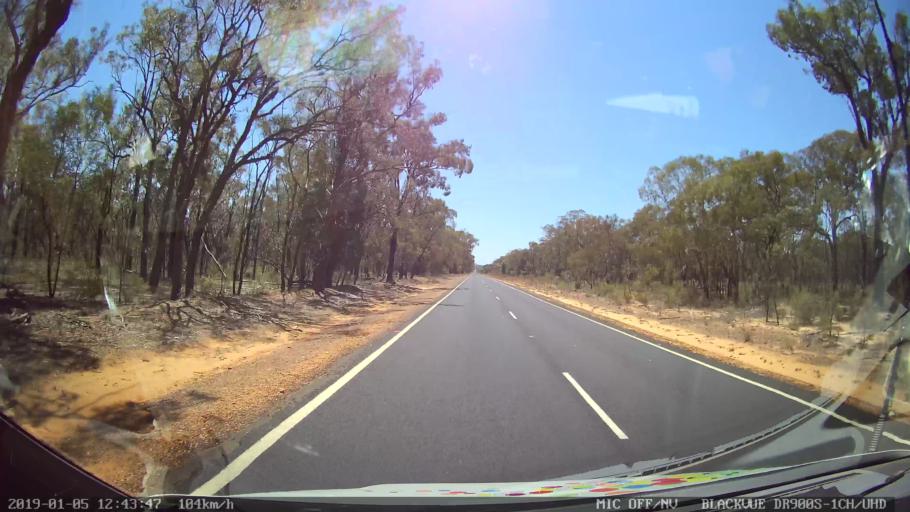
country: AU
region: New South Wales
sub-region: Warrumbungle Shire
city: Coonabarabran
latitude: -31.1445
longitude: 149.5286
